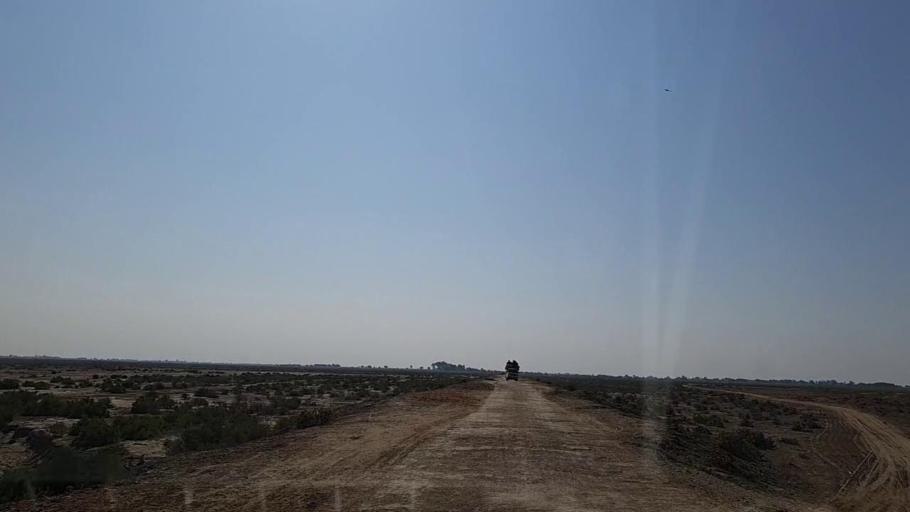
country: PK
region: Sindh
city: Chuhar Jamali
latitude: 24.5102
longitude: 68.0977
